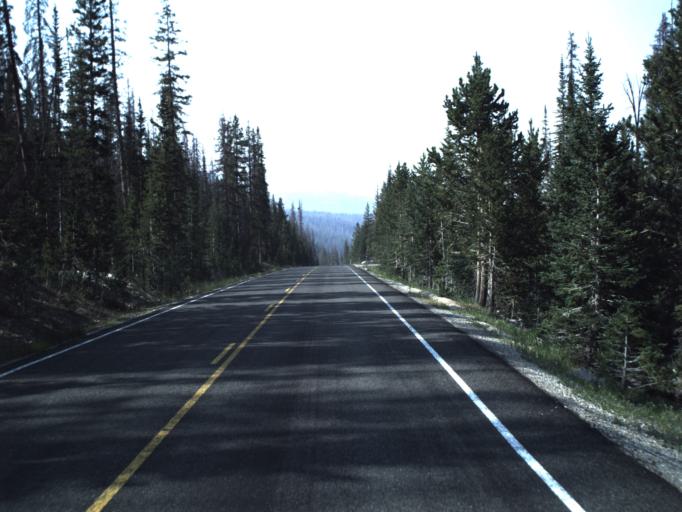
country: US
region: Utah
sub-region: Summit County
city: Kamas
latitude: 40.7502
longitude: -110.8762
